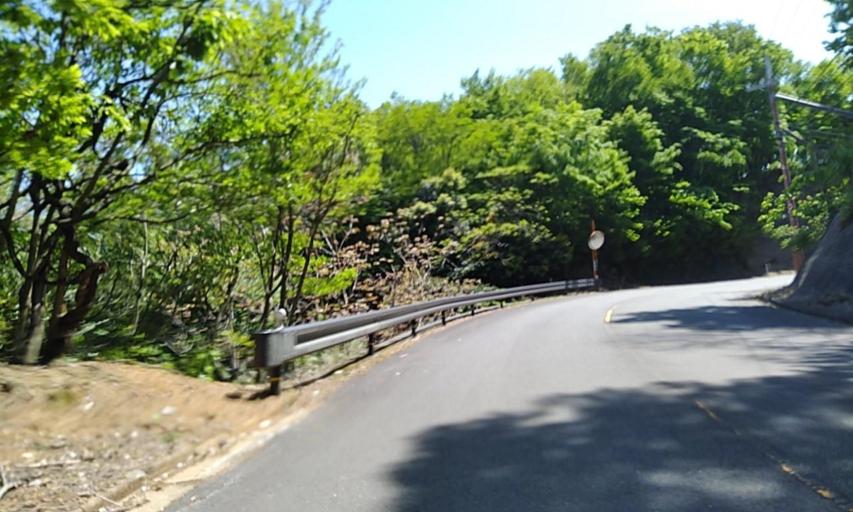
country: JP
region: Fukui
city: Obama
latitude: 35.5420
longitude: 135.7544
